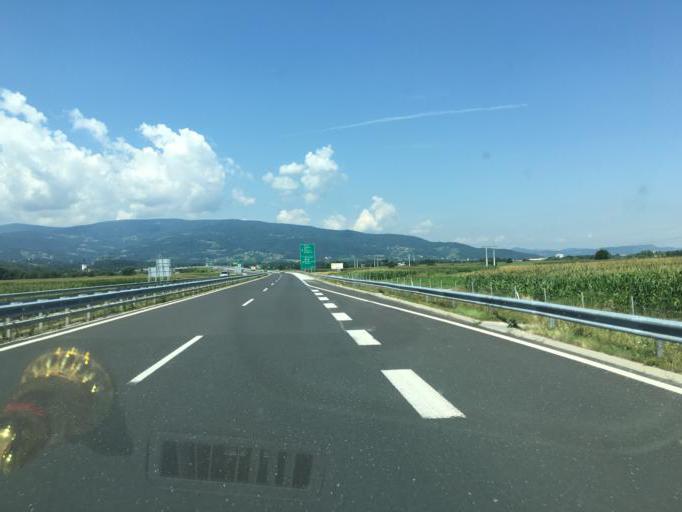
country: SI
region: Hoce-Slivnica
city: Hotinja Vas
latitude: 46.4750
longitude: 15.6743
